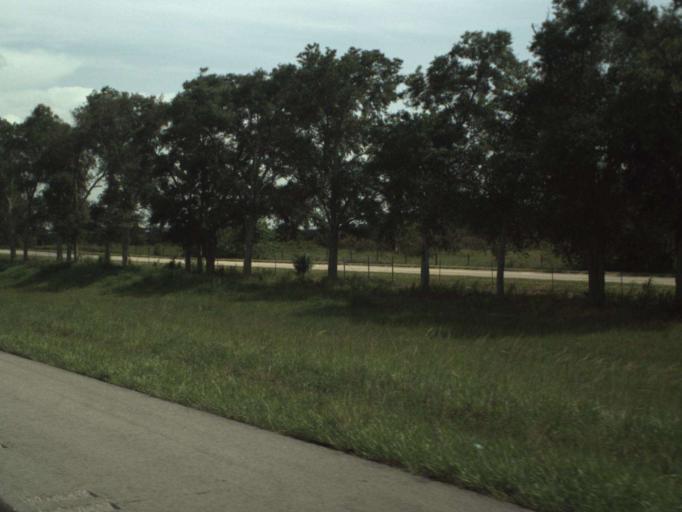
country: US
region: Florida
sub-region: Saint Lucie County
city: Lakewood Park
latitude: 27.5082
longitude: -80.4451
